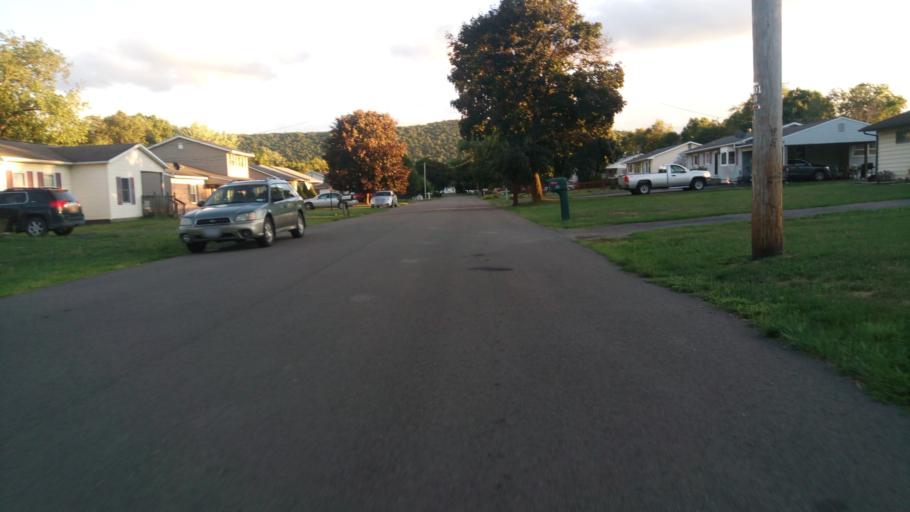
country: US
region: New York
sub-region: Chemung County
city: Southport
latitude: 42.0629
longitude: -76.8028
